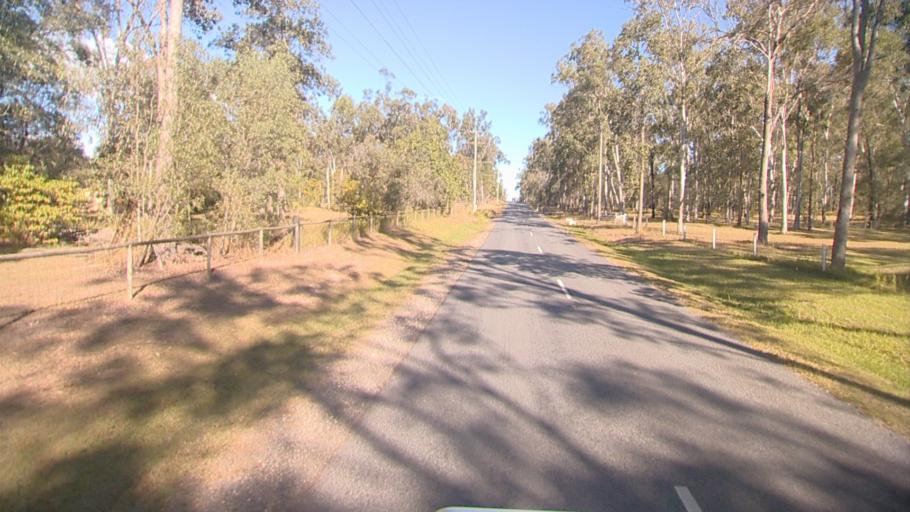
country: AU
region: Queensland
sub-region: Logan
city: Chambers Flat
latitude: -27.8076
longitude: 153.0724
